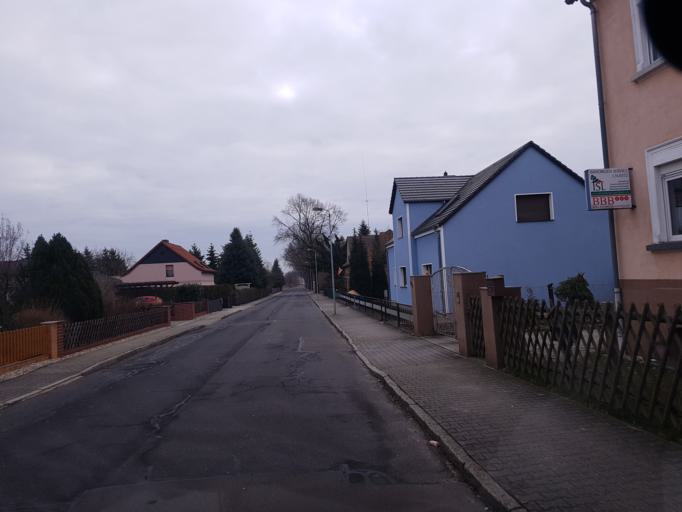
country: DE
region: Brandenburg
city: Senftenberg
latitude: 51.5278
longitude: 13.9571
